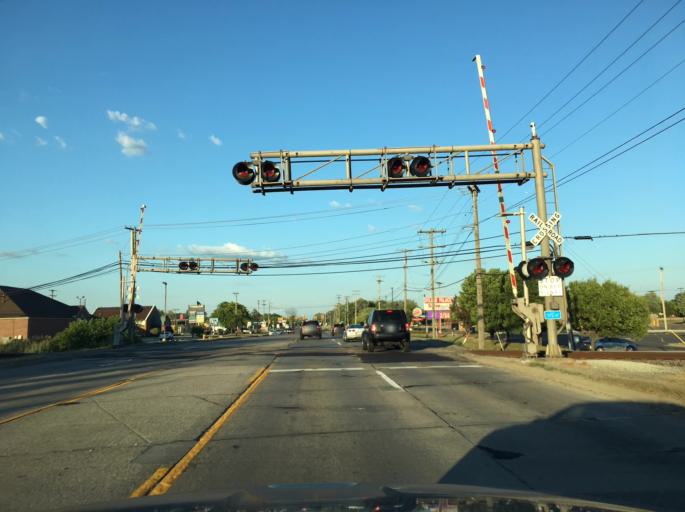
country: US
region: Michigan
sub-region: Macomb County
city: Fraser
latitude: 42.5541
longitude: -82.9270
